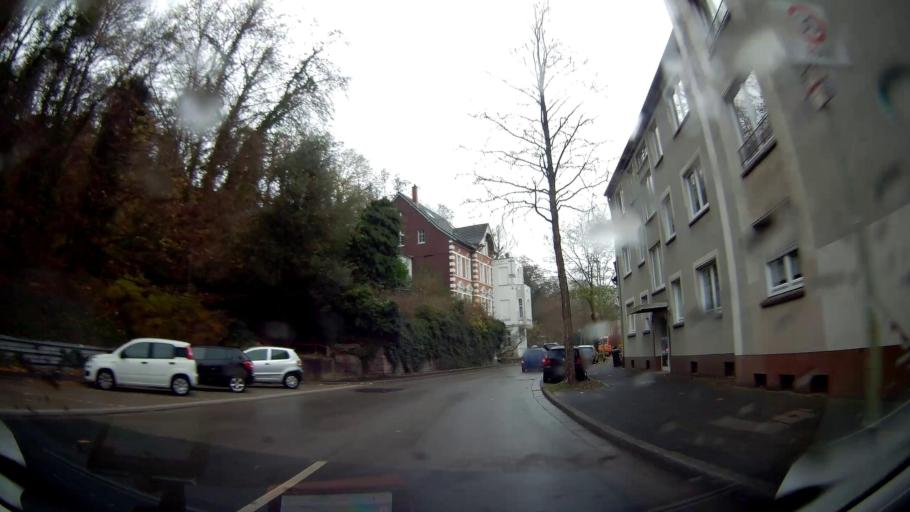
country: DE
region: North Rhine-Westphalia
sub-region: Regierungsbezirk Dusseldorf
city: Essen
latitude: 51.4439
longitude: 7.0696
